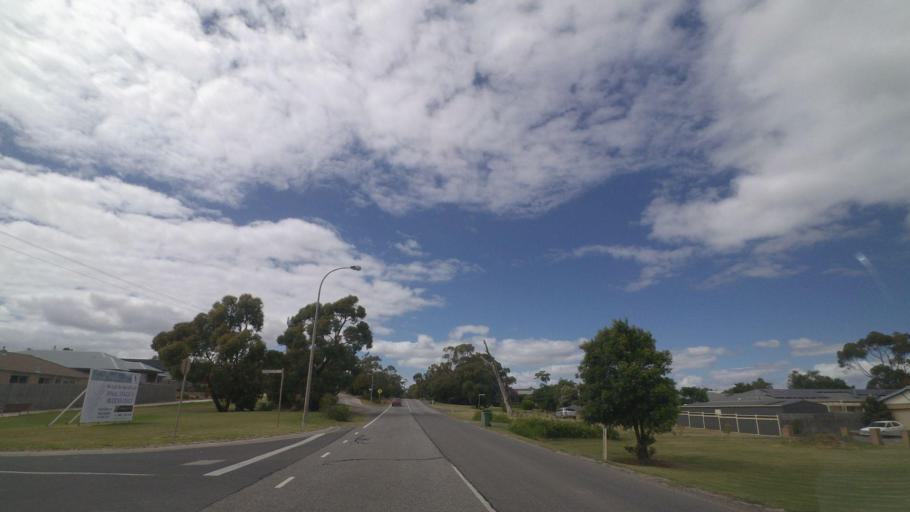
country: AU
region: Victoria
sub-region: Cardinia
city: Koo-Wee-Rup
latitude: -38.2702
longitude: 145.5672
